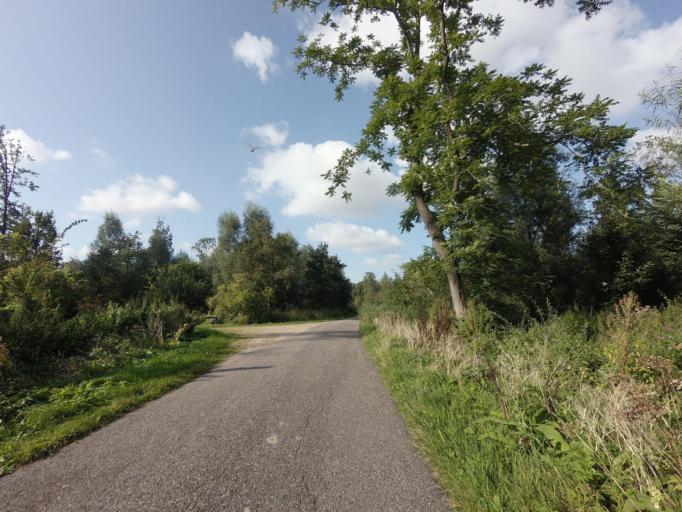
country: NL
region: Flevoland
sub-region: Gemeente Noordoostpolder
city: Ens
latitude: 52.6445
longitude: 5.7728
